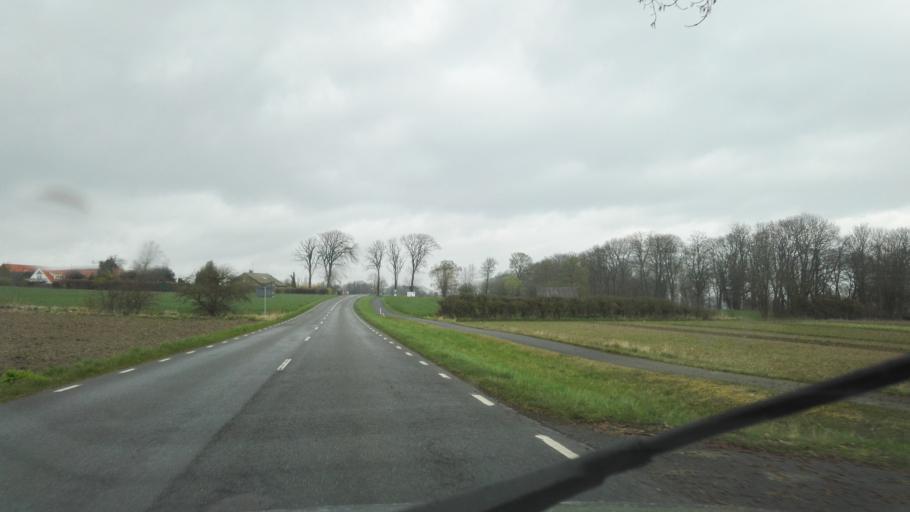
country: SE
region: Skane
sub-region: Simrishamns Kommun
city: Simrishamn
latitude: 55.5000
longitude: 14.3214
